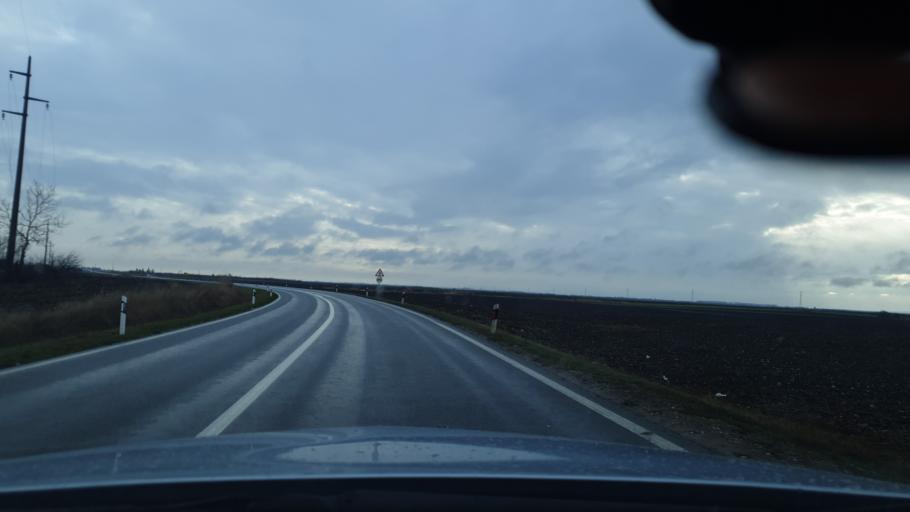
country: RS
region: Autonomna Pokrajina Vojvodina
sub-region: Juznobanatski Okrug
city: Kovin
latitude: 44.8106
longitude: 20.8591
